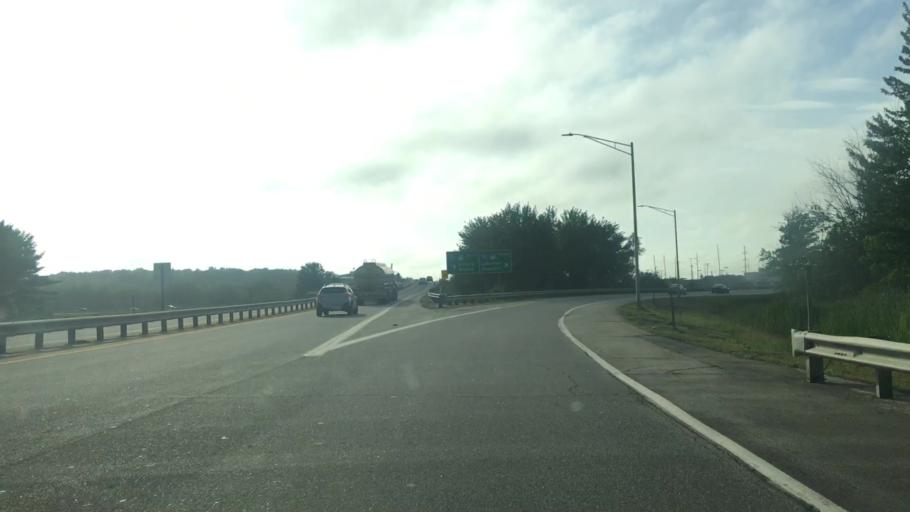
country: US
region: Maine
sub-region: Cumberland County
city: South Portland Gardens
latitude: 43.6311
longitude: -70.3409
